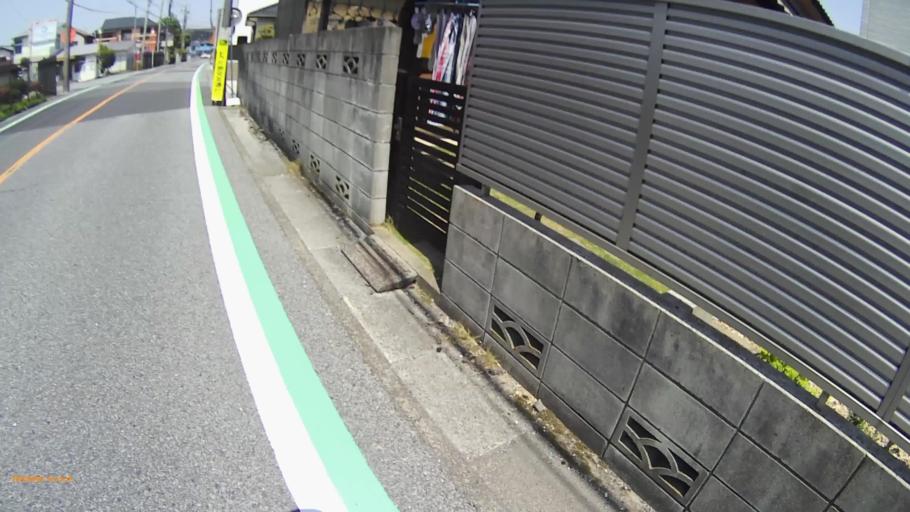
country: JP
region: Saitama
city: Koshigaya
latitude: 35.9193
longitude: 139.7819
